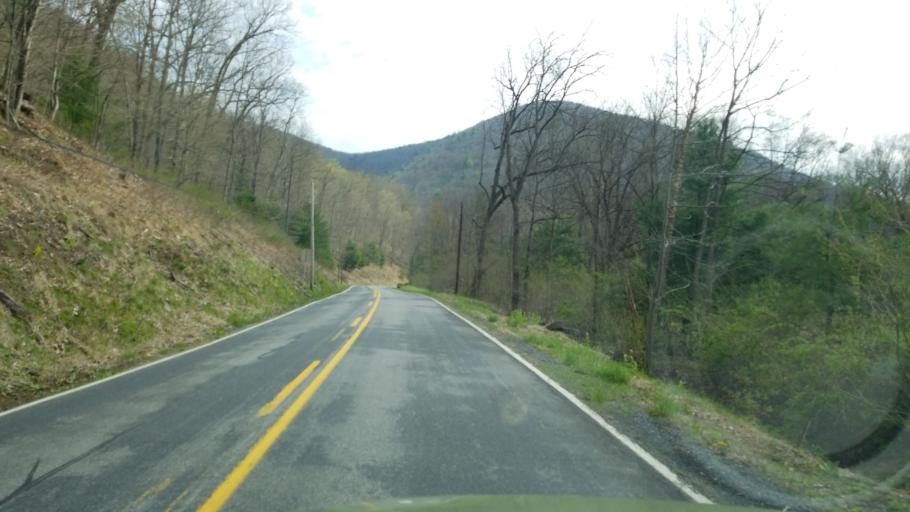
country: US
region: Pennsylvania
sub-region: Clinton County
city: Renovo
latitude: 41.2994
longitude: -78.0216
